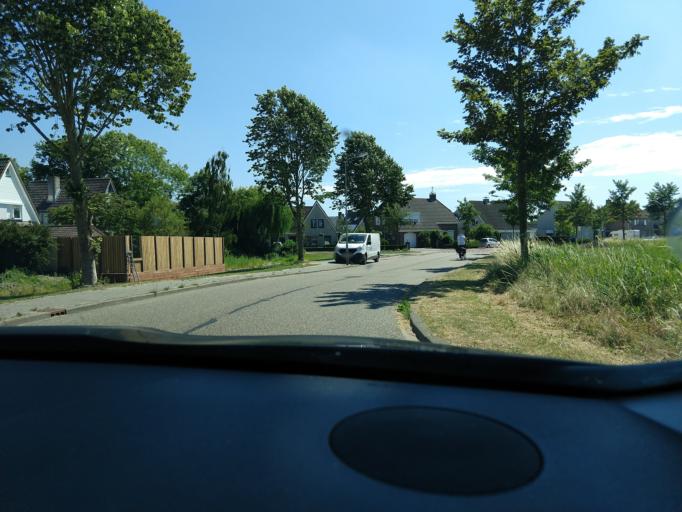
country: NL
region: Zeeland
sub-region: Gemeente Veere
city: Veere
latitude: 51.5056
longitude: 3.6713
